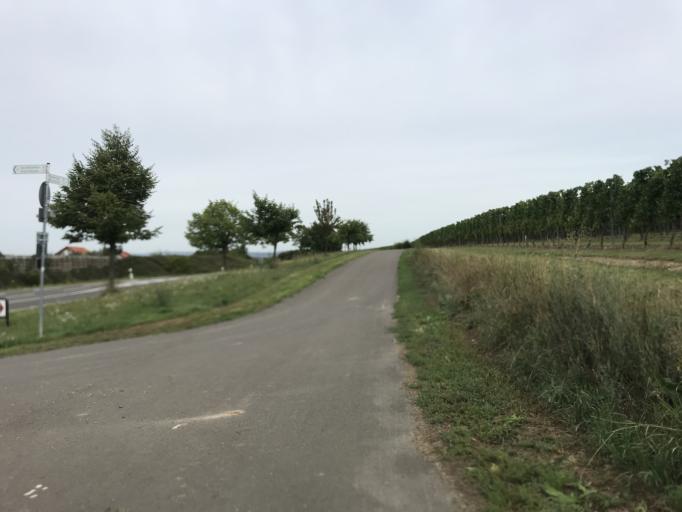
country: DE
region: Rheinland-Pfalz
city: Sprendlingen
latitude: 49.8676
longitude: 7.9855
